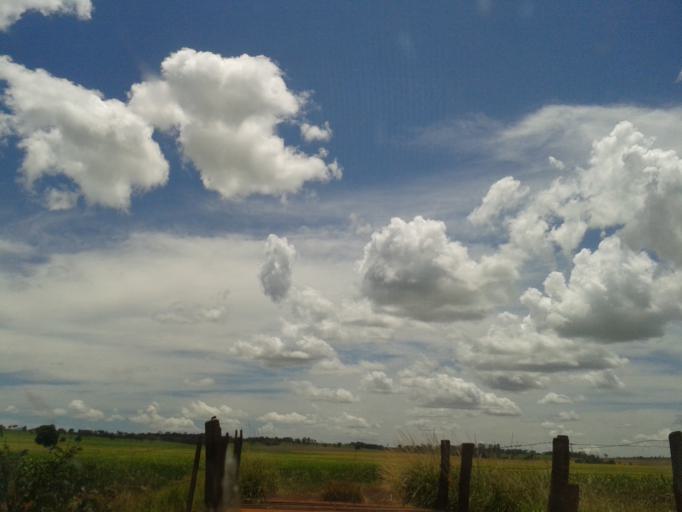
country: BR
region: Minas Gerais
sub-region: Capinopolis
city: Capinopolis
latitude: -18.7758
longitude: -49.8039
